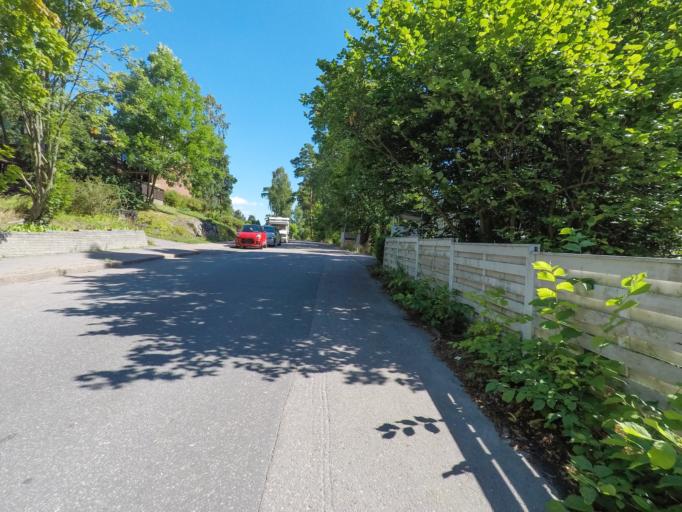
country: FI
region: Uusimaa
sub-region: Helsinki
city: Vantaa
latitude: 60.1904
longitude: 25.0686
